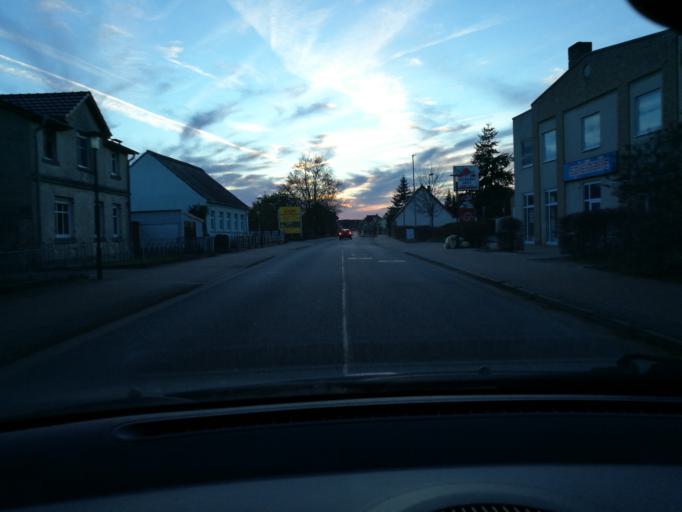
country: DE
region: Brandenburg
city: Lenzen
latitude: 53.0934
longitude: 11.4820
